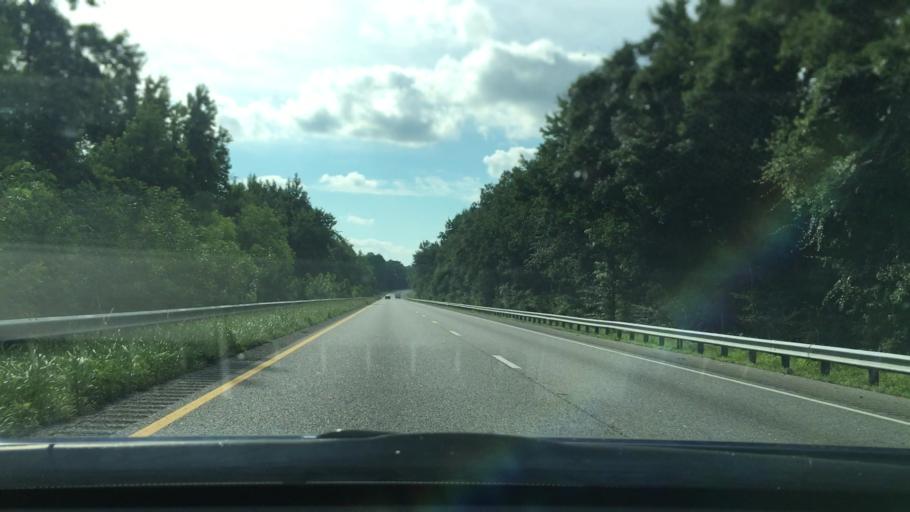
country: US
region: South Carolina
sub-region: Dorchester County
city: Ridgeville
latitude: 33.1507
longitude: -80.3381
